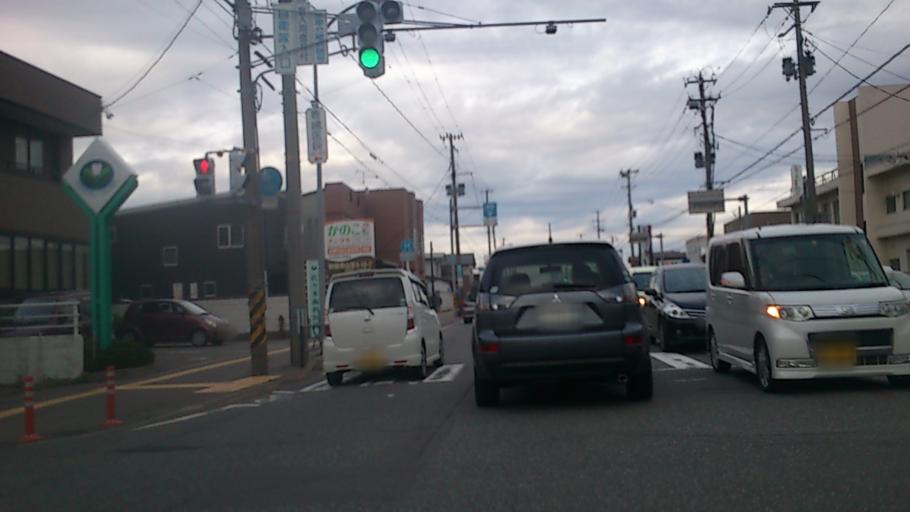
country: JP
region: Akita
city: Akita Shi
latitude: 39.7476
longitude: 140.0797
